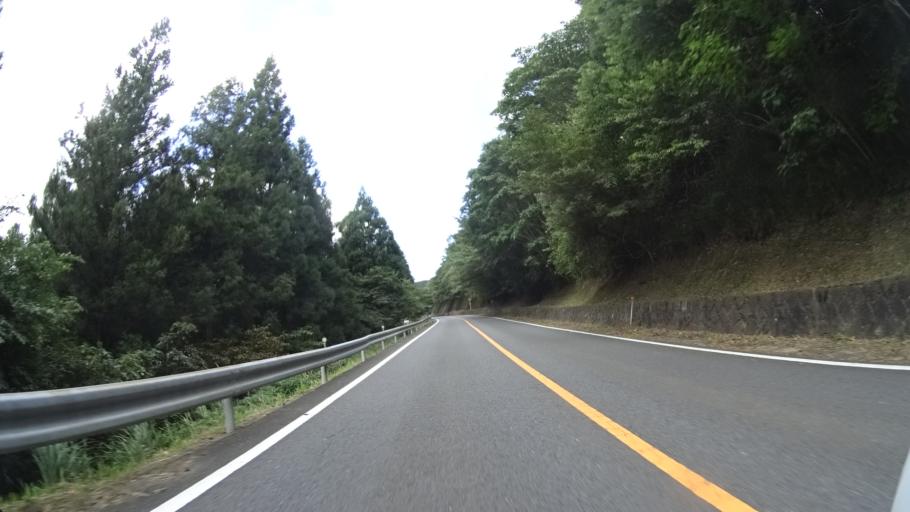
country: JP
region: Oita
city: Tsukawaki
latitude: 33.2472
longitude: 131.2931
